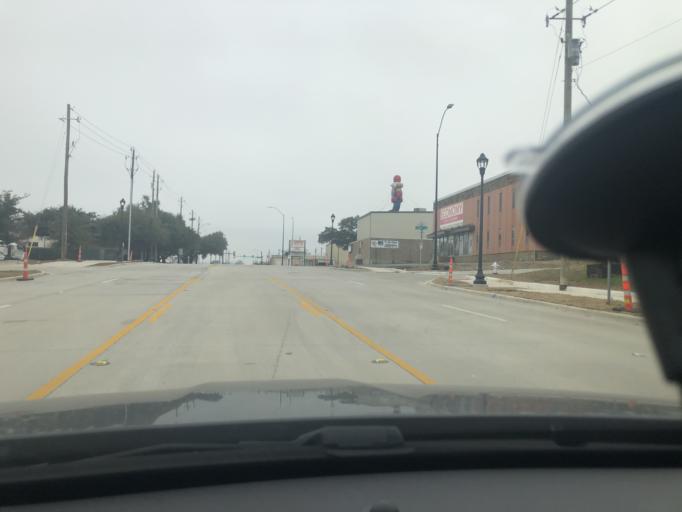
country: US
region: Texas
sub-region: Tarrant County
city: Westworth
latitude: 32.7382
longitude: -97.3700
